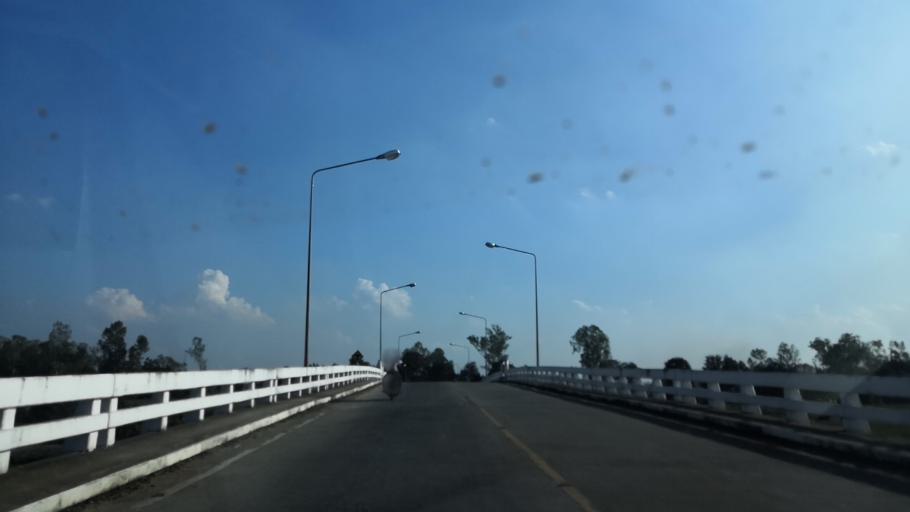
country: TH
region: Chiang Rai
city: Wiang Chai
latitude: 19.9611
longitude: 99.9456
